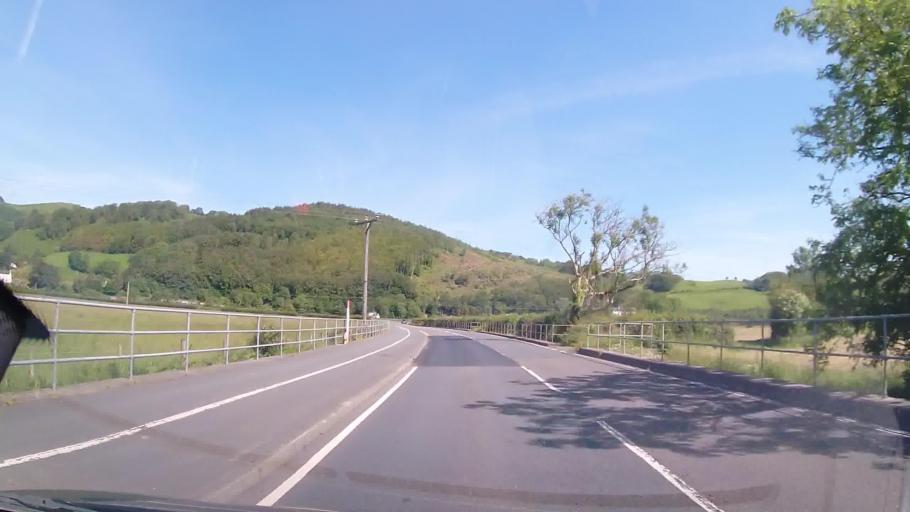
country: GB
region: Wales
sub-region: Sir Powys
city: Machynlleth
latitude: 52.5967
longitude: -3.8555
